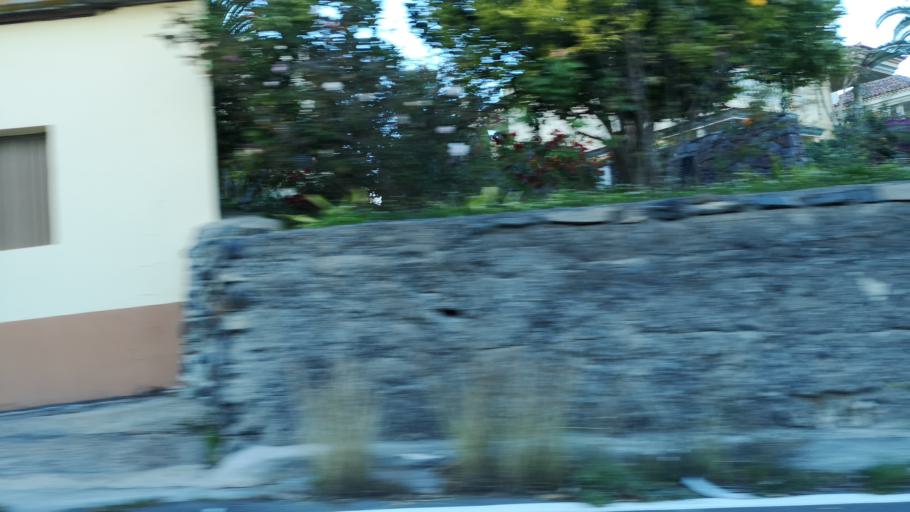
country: ES
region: Canary Islands
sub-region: Provincia de Santa Cruz de Tenerife
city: Alajero
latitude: 28.0572
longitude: -17.2337
